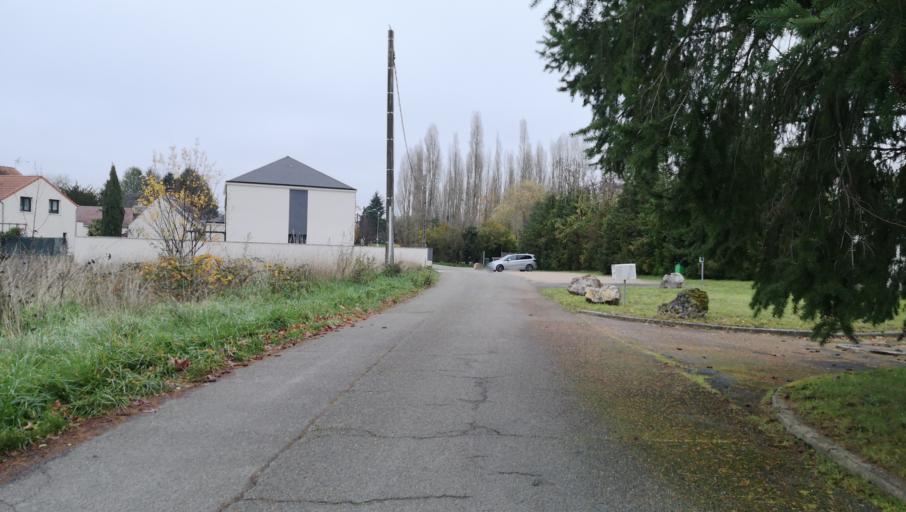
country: FR
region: Centre
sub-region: Departement du Loiret
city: Semoy
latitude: 47.9255
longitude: 1.9640
